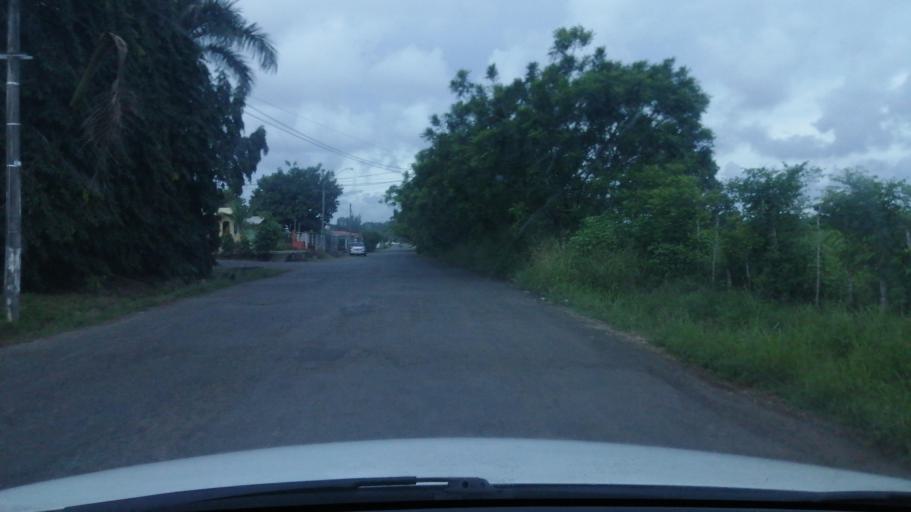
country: PA
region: Chiriqui
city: David
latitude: 8.4049
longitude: -82.4514
